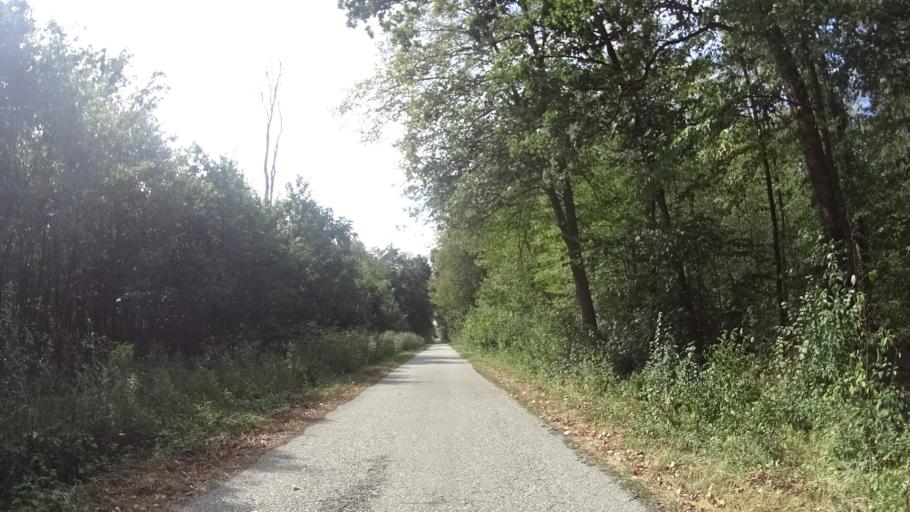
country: CZ
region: Olomoucky
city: Naklo
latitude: 49.6832
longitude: 17.1391
